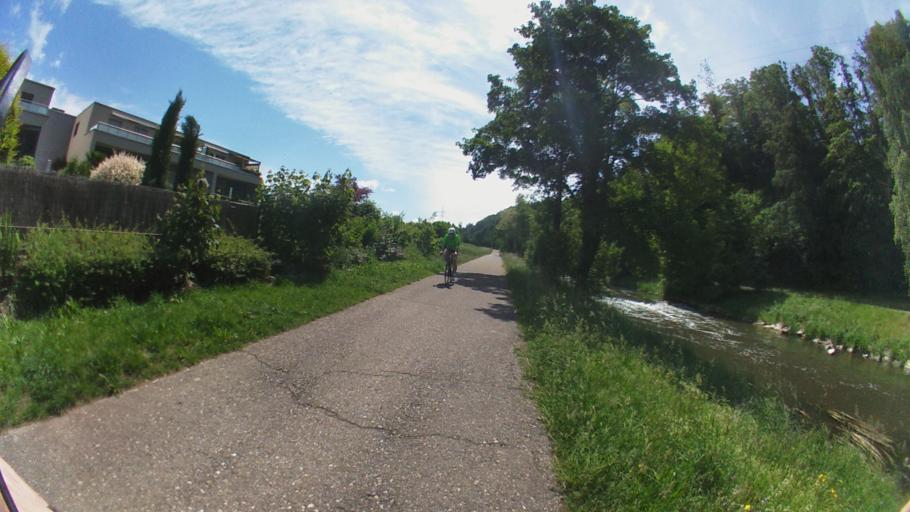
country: CH
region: Zurich
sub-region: Bezirk Buelach
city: Glattfelden
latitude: 47.5541
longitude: 8.5012
